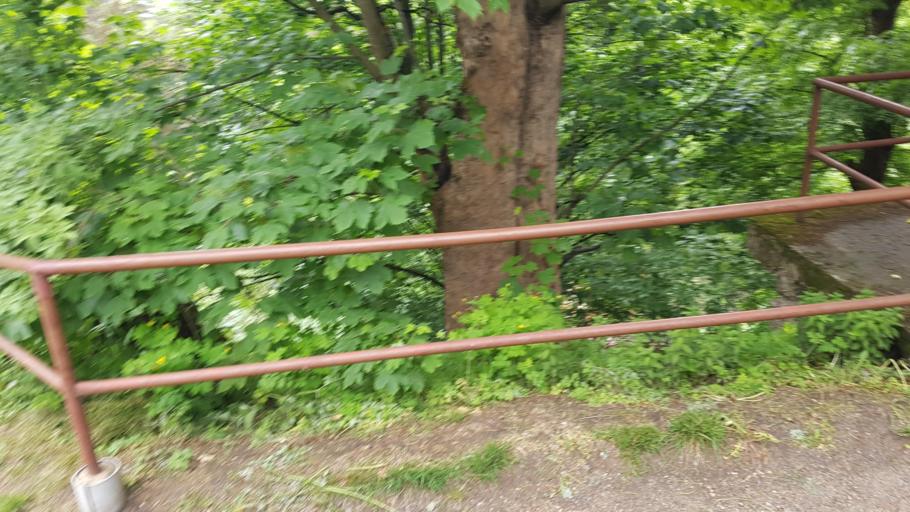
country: DE
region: Saxony
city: Kurort Jonsdorf
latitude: 50.8508
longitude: 14.6835
